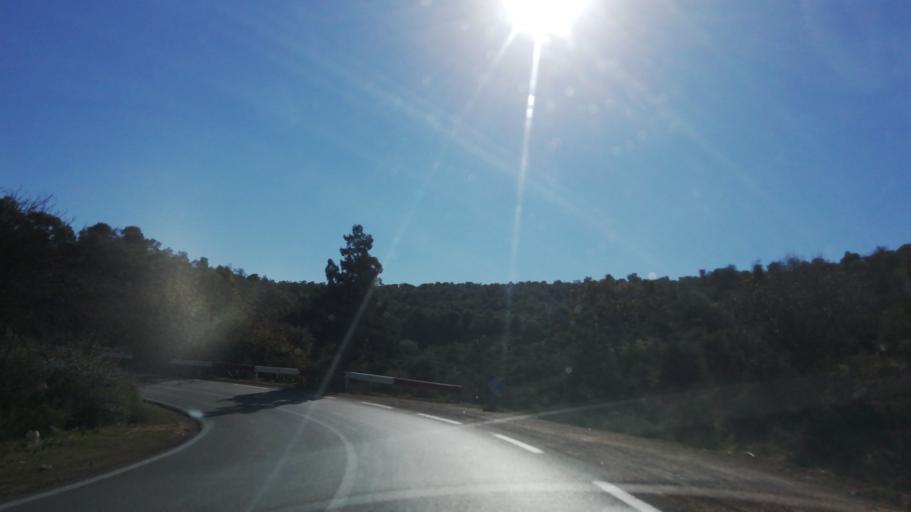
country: DZ
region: Tlemcen
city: Beni Mester
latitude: 34.8183
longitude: -1.6365
